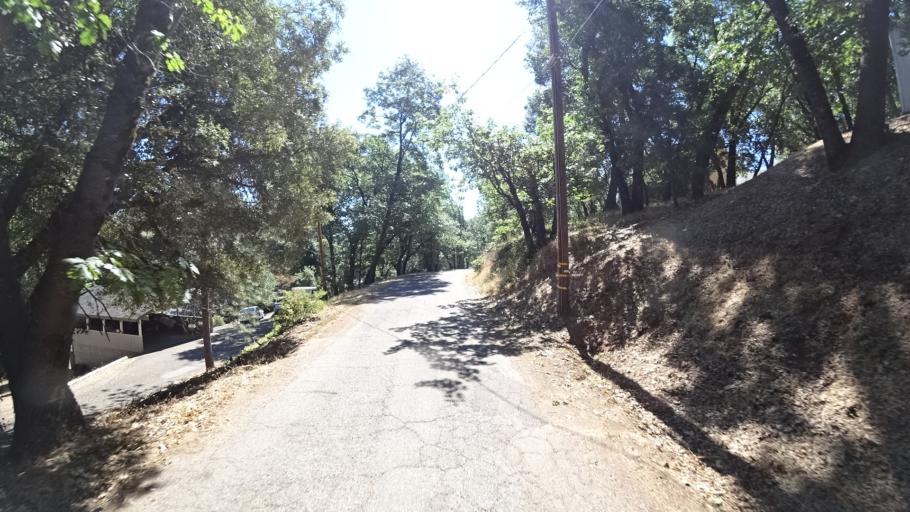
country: US
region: California
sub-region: Calaveras County
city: Forest Meadows
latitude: 38.1739
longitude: -120.3782
